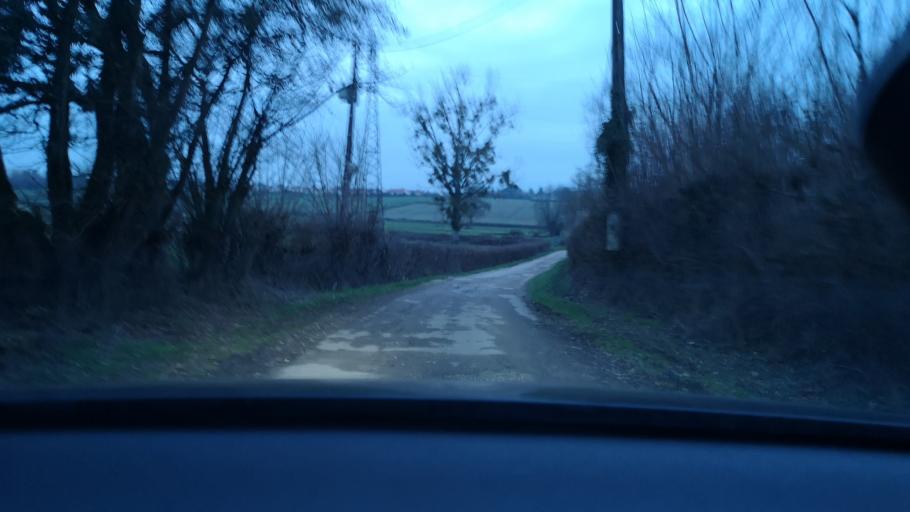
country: FR
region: Bourgogne
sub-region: Departement de Saone-et-Loire
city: Saint-Remy
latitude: 46.7634
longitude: 4.8057
